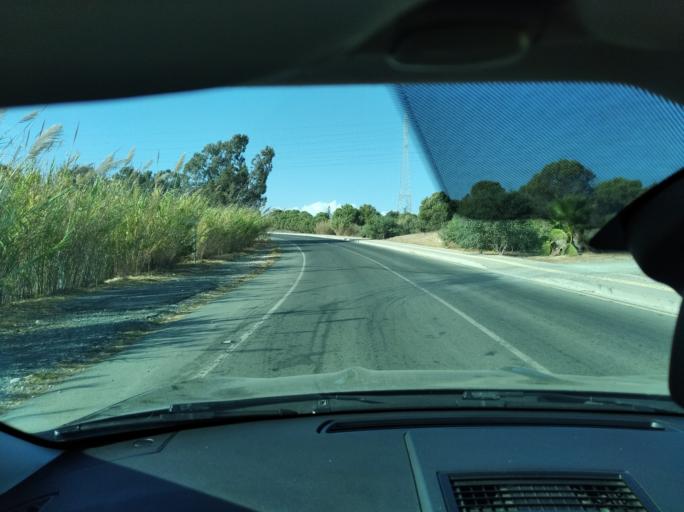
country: CY
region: Larnaka
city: Xylotymbou
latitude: 35.0005
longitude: 33.7627
